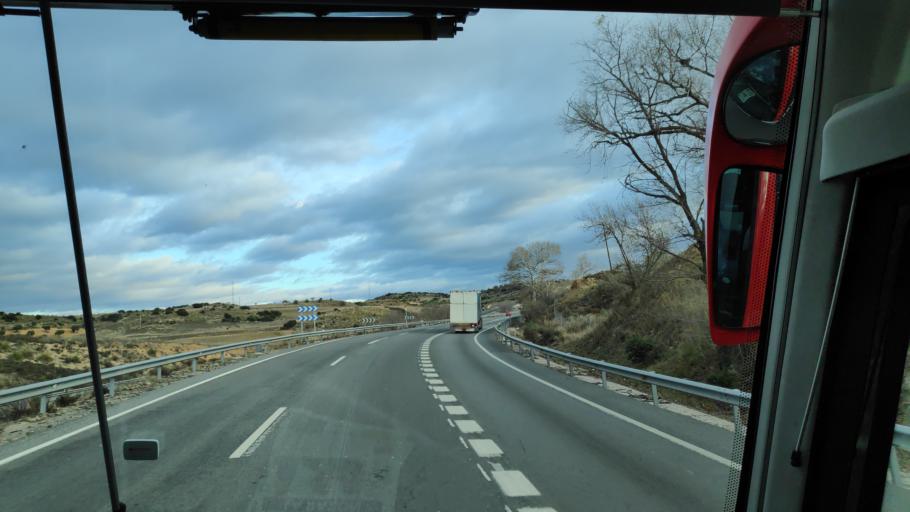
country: ES
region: Madrid
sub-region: Provincia de Madrid
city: Villarejo de Salvanes
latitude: 40.1976
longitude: -3.3085
